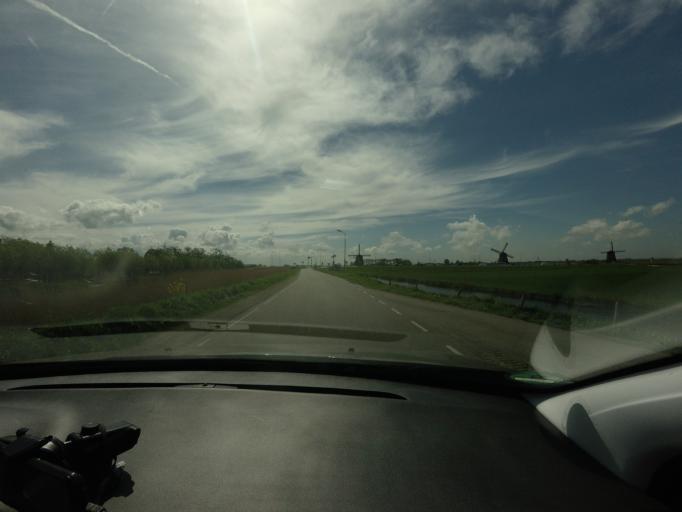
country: NL
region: North Holland
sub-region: Gemeente Heerhugowaard
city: Heerhugowaard
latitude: 52.6016
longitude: 4.8779
